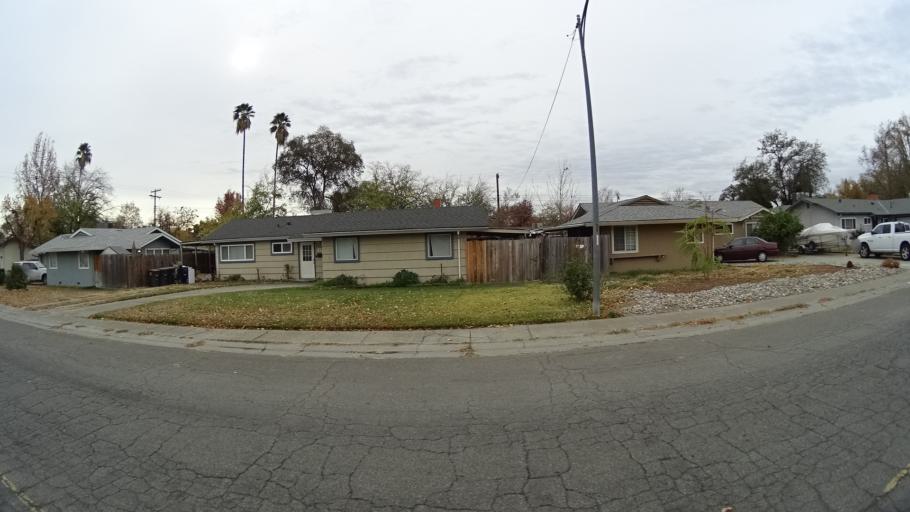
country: US
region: California
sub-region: Sacramento County
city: Citrus Heights
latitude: 38.7106
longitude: -121.2933
